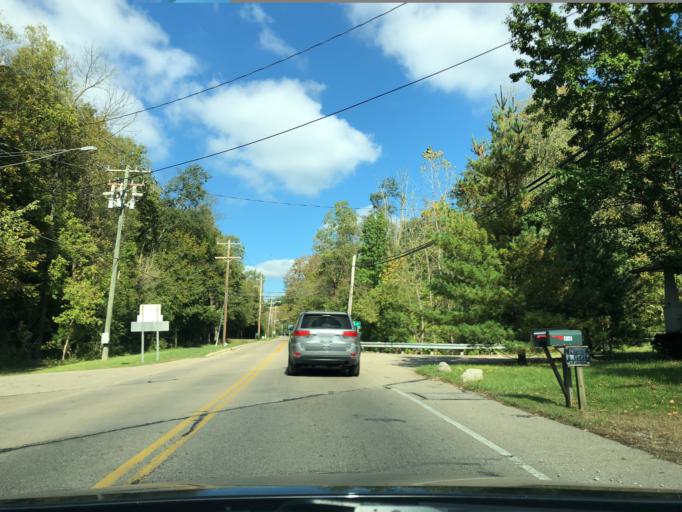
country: US
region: Ohio
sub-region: Hamilton County
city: Loveland
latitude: 39.2701
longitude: -84.2543
